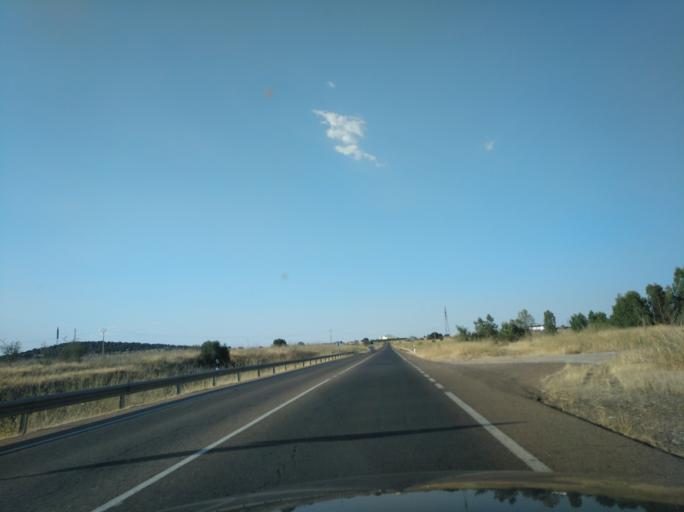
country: ES
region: Extremadura
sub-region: Provincia de Badajoz
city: Olivenza
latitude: 38.6980
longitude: -7.0897
